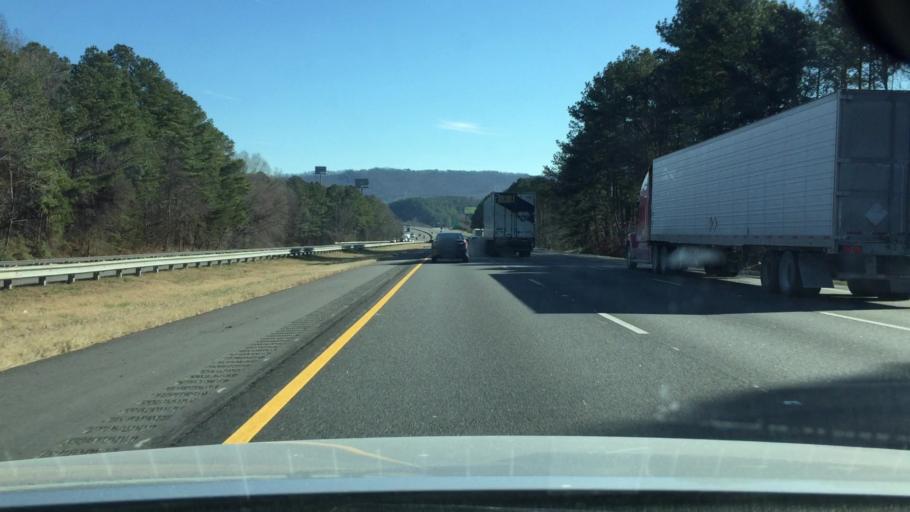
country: US
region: Georgia
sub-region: Whitfield County
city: Varnell
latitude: 34.8688
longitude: -85.0366
